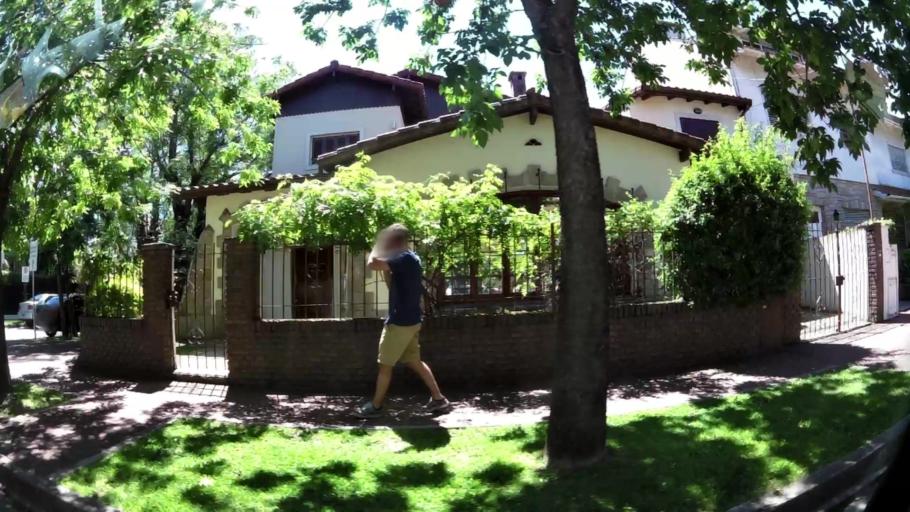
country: AR
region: Buenos Aires
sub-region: Partido de San Isidro
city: San Isidro
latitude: -34.4790
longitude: -58.5020
